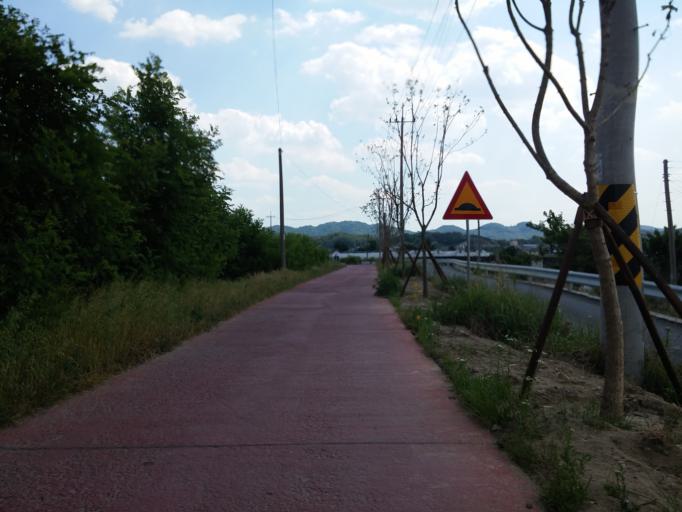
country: KR
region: Chungcheongbuk-do
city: Cheongju-si
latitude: 36.5940
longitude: 127.4969
